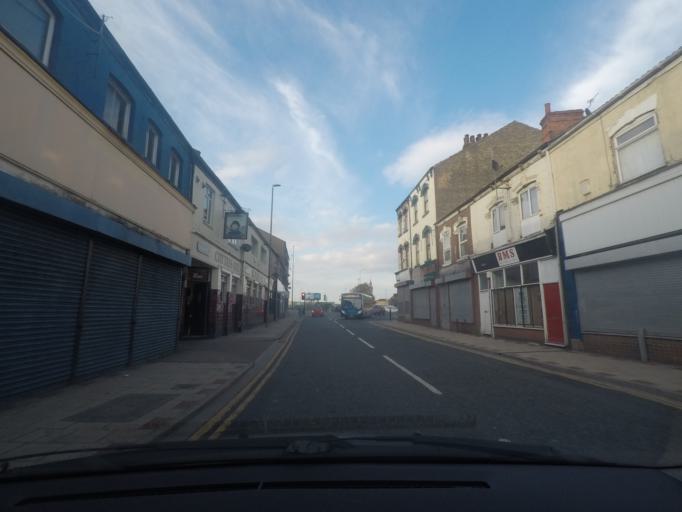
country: GB
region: England
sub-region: North East Lincolnshire
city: Grimsby
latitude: 53.5744
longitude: -0.0728
